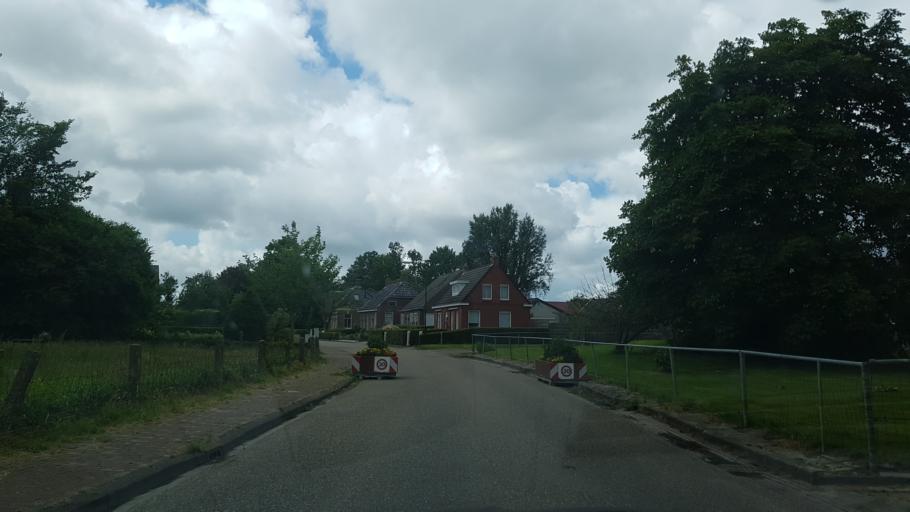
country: NL
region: Groningen
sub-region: Gemeente Winsum
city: Winsum
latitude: 53.3996
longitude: 6.4885
